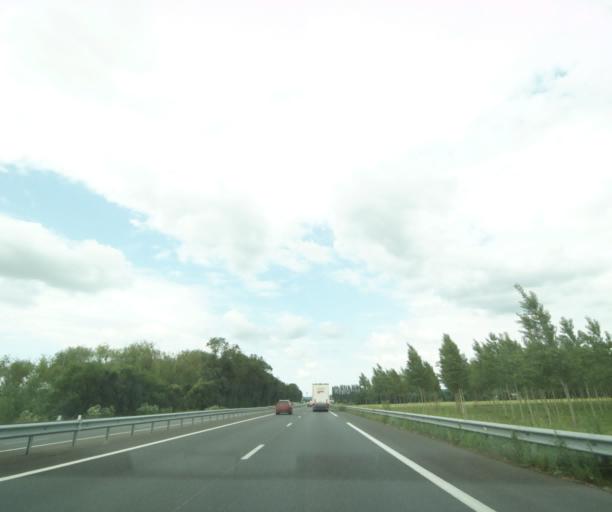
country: FR
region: Pays de la Loire
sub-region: Departement de Maine-et-Loire
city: Vivy
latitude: 47.2986
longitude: -0.0390
